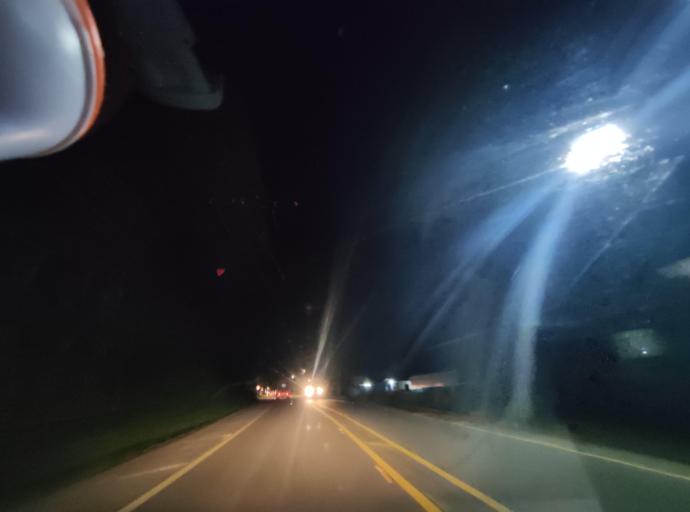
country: IN
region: Kerala
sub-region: Thiruvananthapuram
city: Attingal
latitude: 8.7572
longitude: 76.8926
